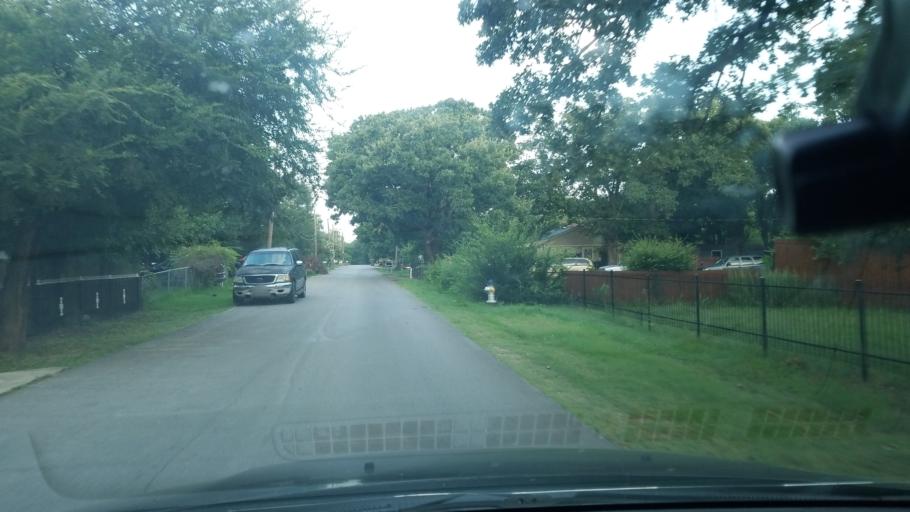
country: US
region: Texas
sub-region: Dallas County
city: Balch Springs
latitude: 32.7286
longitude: -96.6587
